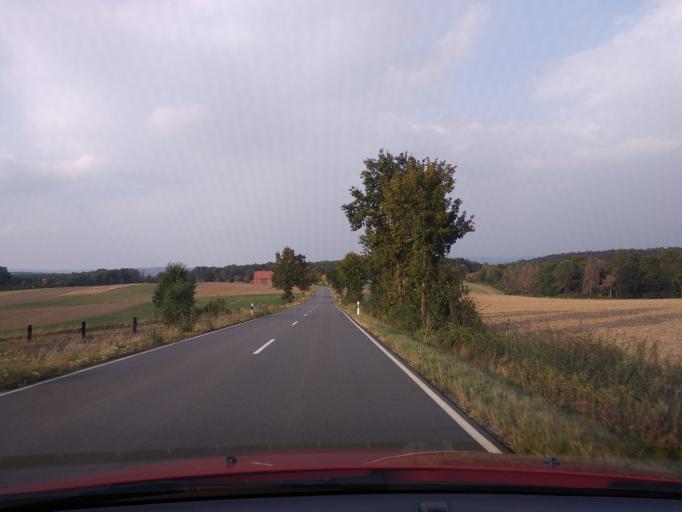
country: DE
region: North Rhine-Westphalia
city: Beverungen
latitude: 51.6357
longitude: 9.3403
